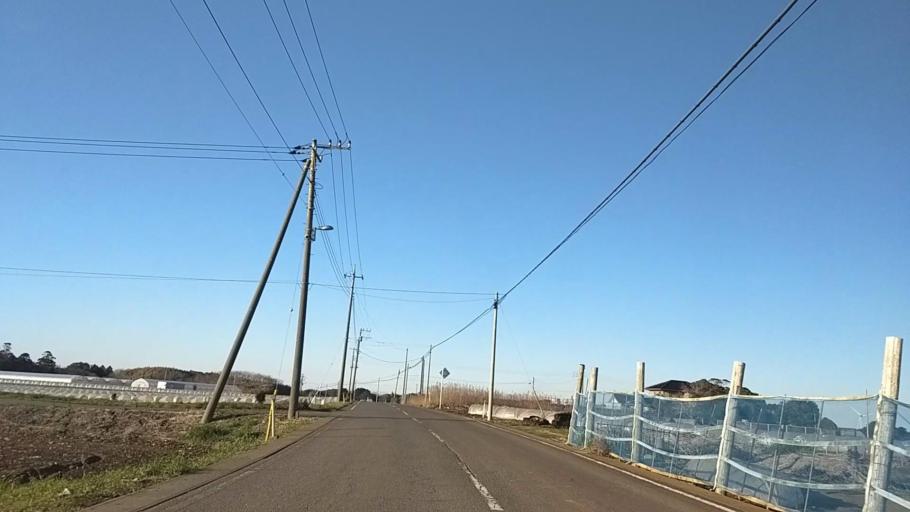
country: JP
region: Chiba
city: Asahi
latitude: 35.7378
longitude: 140.7378
